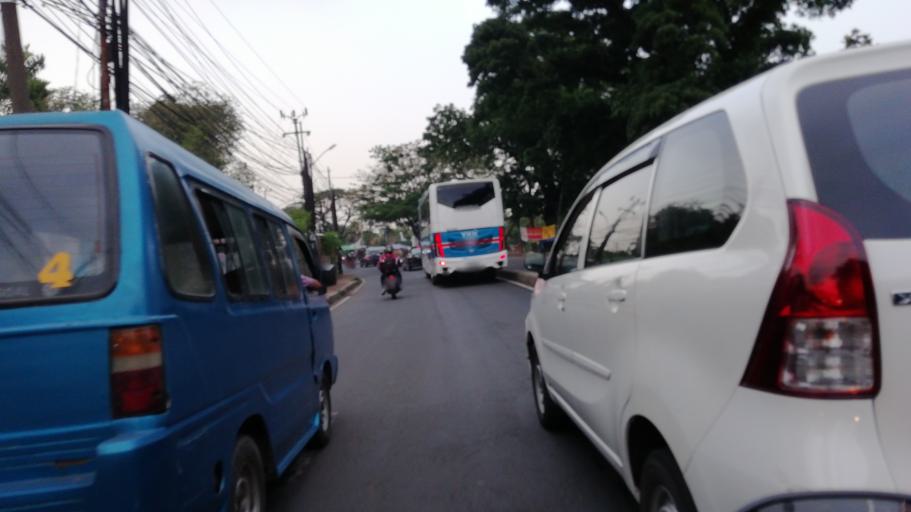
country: ID
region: West Java
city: Cibinong
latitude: -6.4587
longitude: 106.8561
